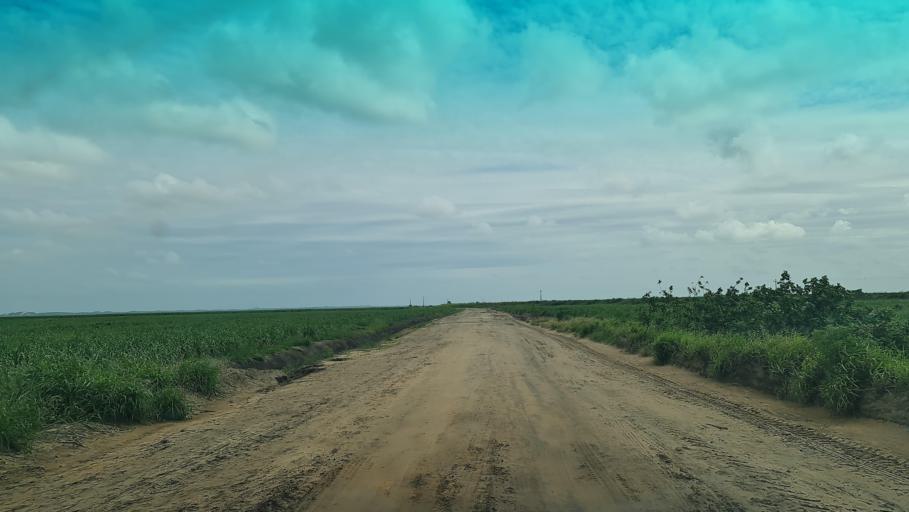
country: MZ
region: Maputo
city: Manhica
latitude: -25.4571
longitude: 32.8189
